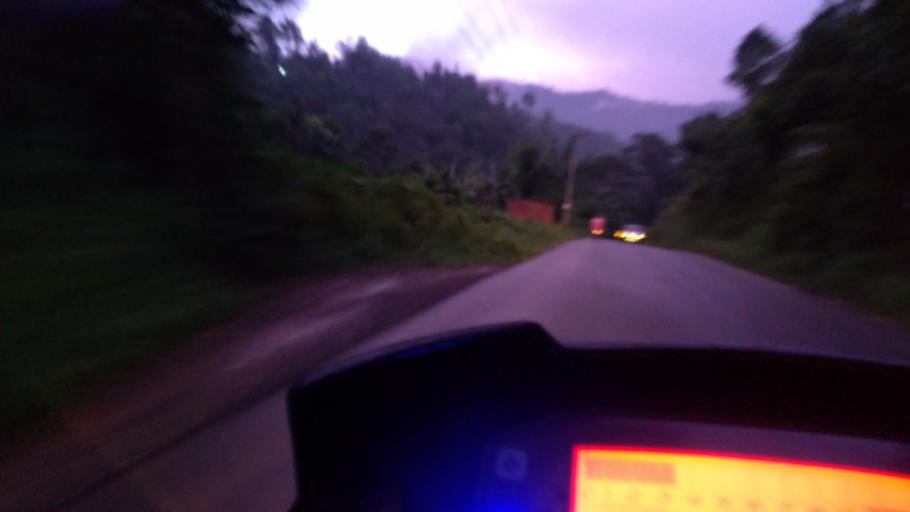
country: IN
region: Kerala
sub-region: Idukki
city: Munnar
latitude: 9.9730
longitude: 77.0587
